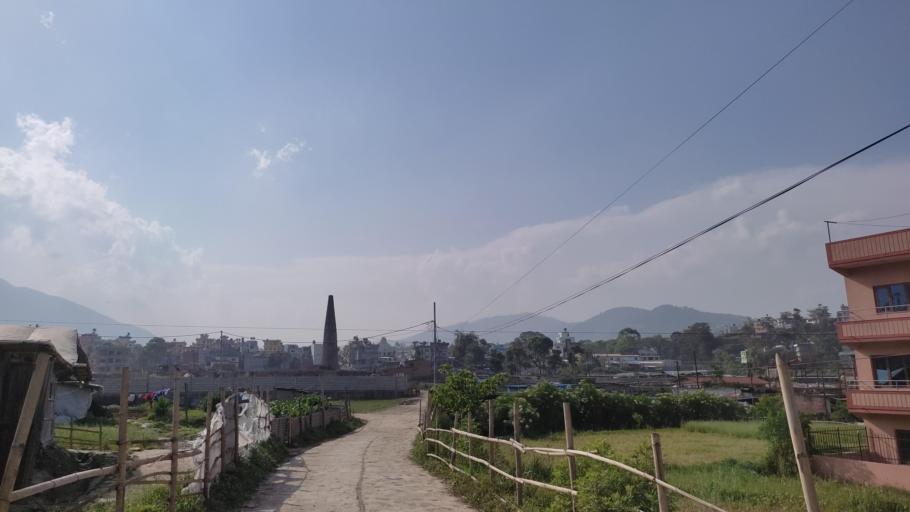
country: NP
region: Central Region
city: Kirtipur
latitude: 27.6787
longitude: 85.2642
